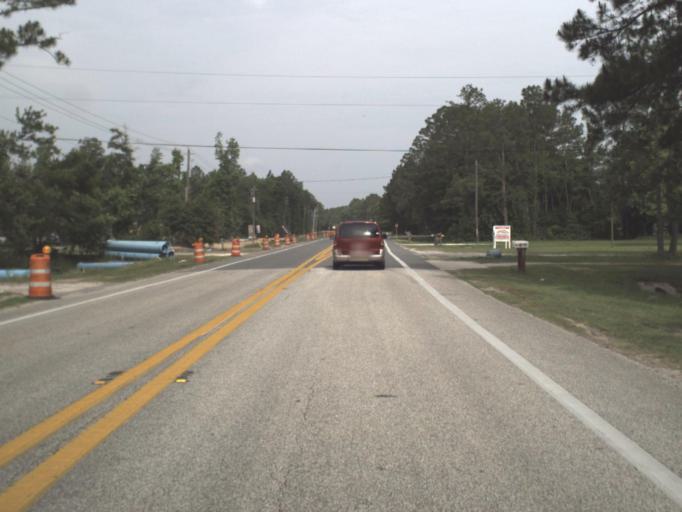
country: US
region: Florida
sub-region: Saint Johns County
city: Saint Augustine
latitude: 29.9589
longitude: -81.4658
